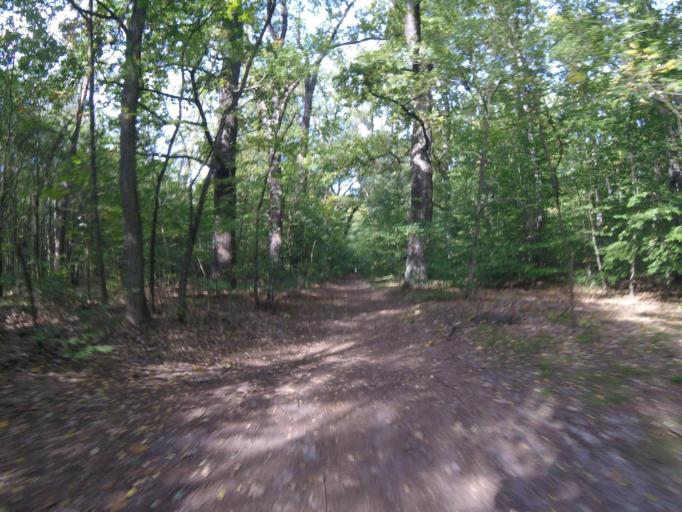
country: DE
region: Brandenburg
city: Konigs Wusterhausen
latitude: 52.2914
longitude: 13.6505
